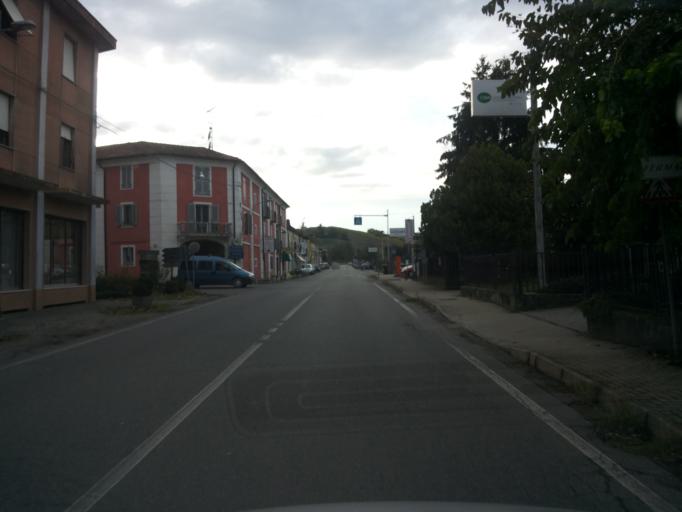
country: IT
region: Piedmont
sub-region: Provincia di Alessandria
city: San Giorgio
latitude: 45.1017
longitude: 8.4109
